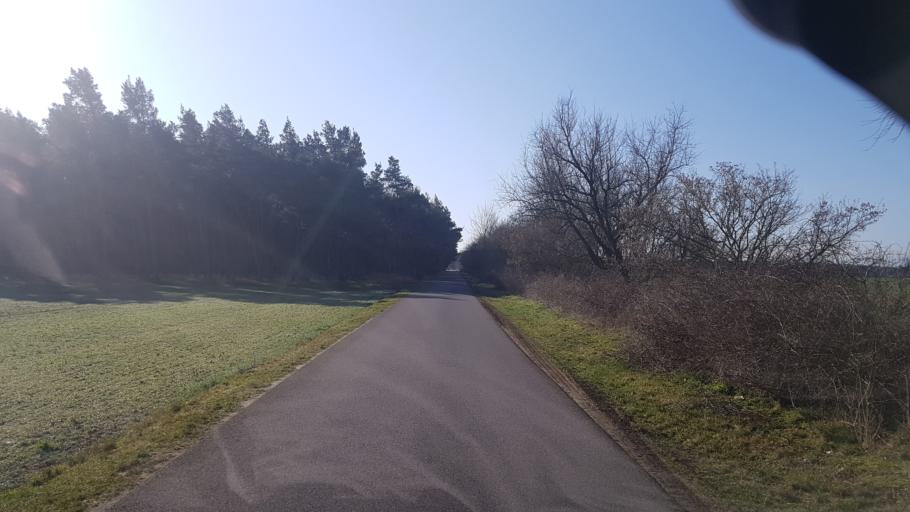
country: DE
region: Brandenburg
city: Luckau
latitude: 51.8490
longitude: 13.7846
